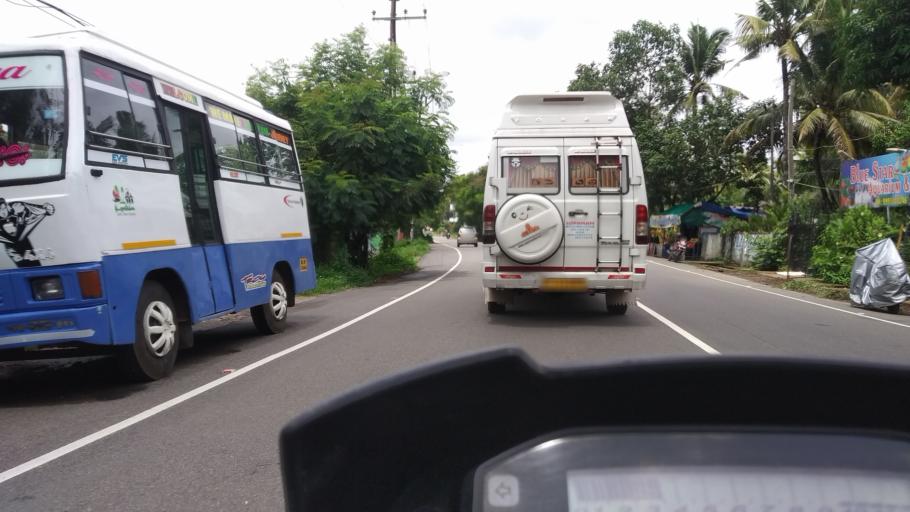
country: IN
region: Kerala
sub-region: Ernakulam
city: Elur
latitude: 10.1366
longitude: 76.2701
